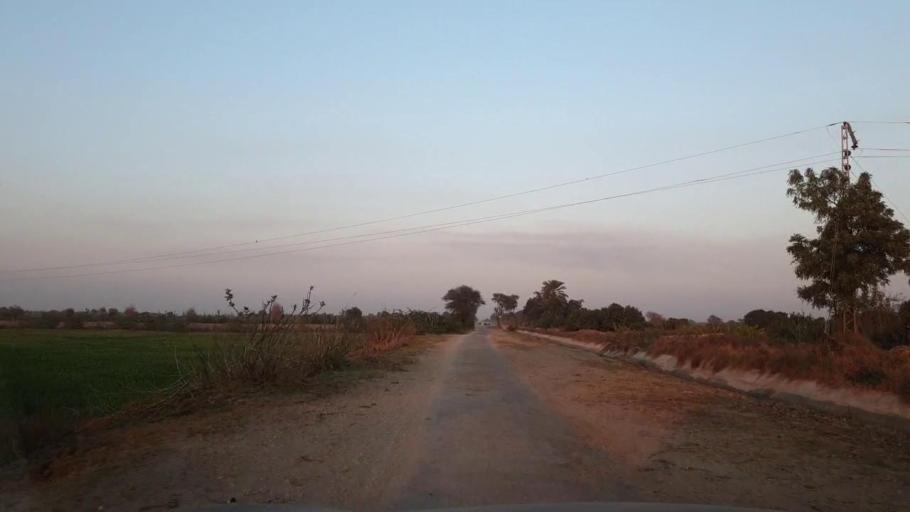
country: PK
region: Sindh
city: Berani
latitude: 25.6616
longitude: 68.7794
